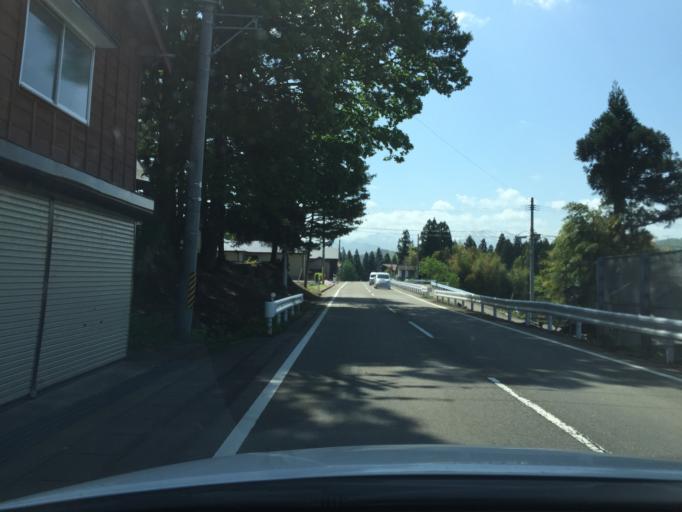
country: JP
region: Niigata
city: Tochio-honcho
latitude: 37.5546
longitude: 139.0785
